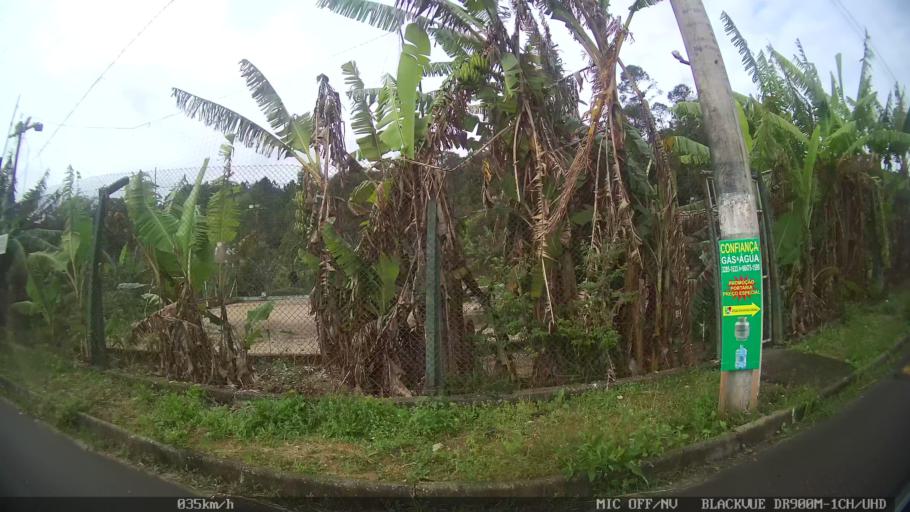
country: BR
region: Santa Catarina
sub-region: Biguacu
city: Biguacu
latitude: -27.5150
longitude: -48.6423
